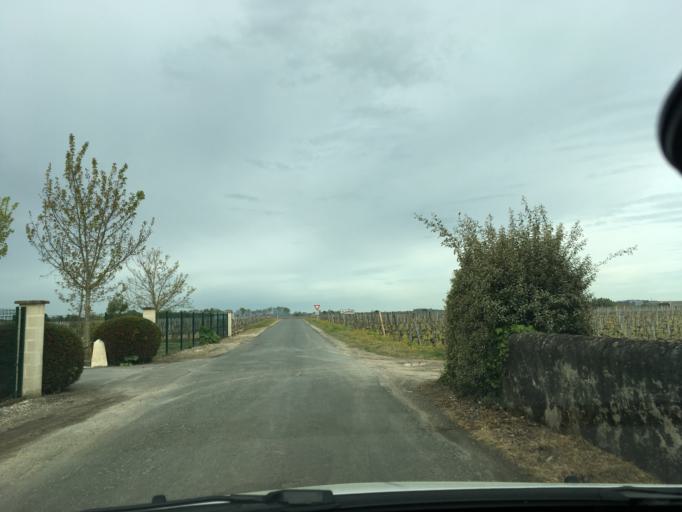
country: FR
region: Aquitaine
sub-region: Departement de la Gironde
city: Lesparre-Medoc
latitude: 45.3250
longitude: -0.8811
